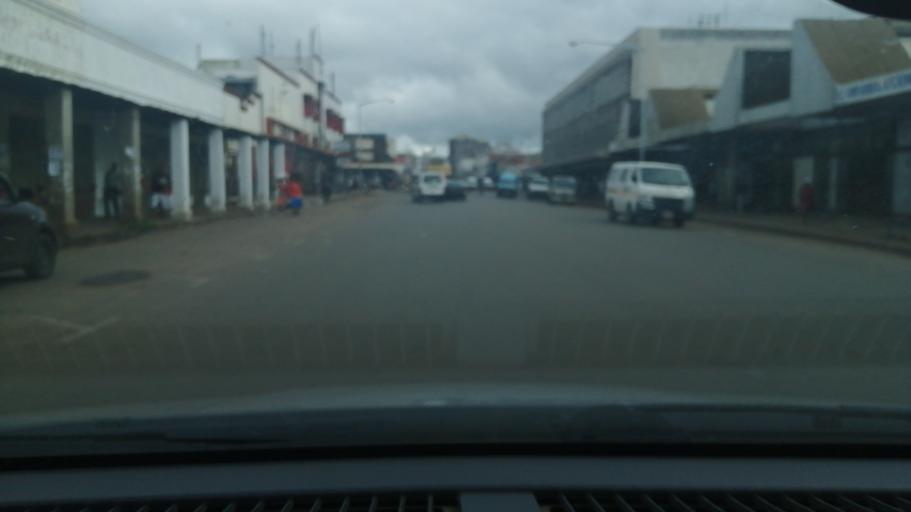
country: ZW
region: Harare
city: Harare
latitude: -17.8389
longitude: 31.0441
